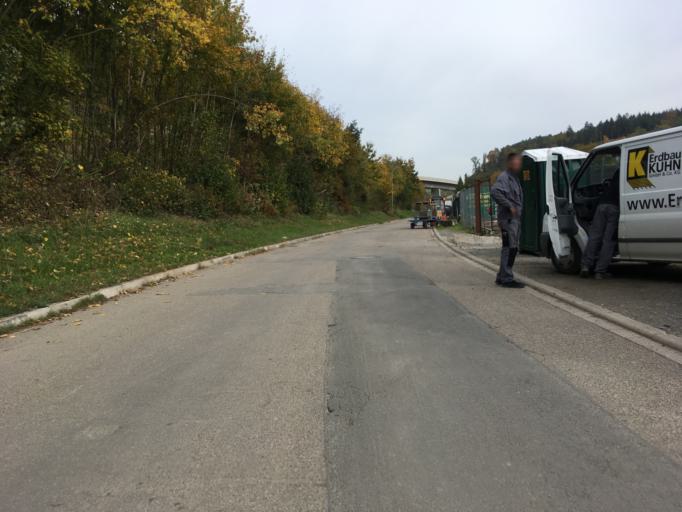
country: DE
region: Baden-Wuerttemberg
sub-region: Karlsruhe Region
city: Adelsheim
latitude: 49.4128
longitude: 9.3863
